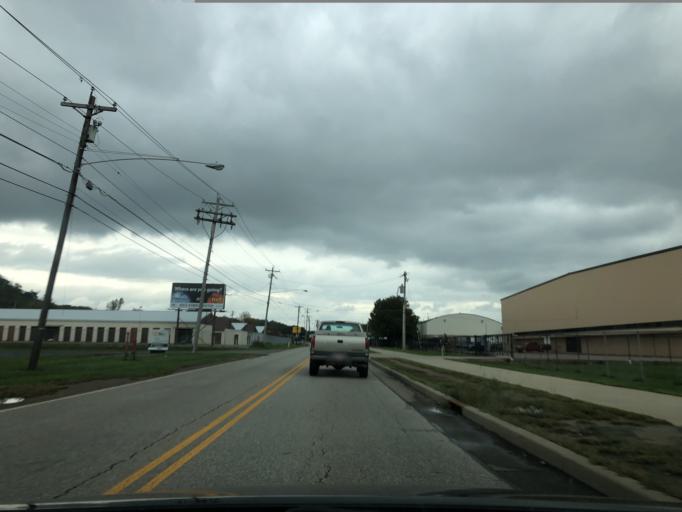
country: US
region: Ohio
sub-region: Hamilton County
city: Turpin Hills
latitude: 39.1090
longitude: -84.4214
